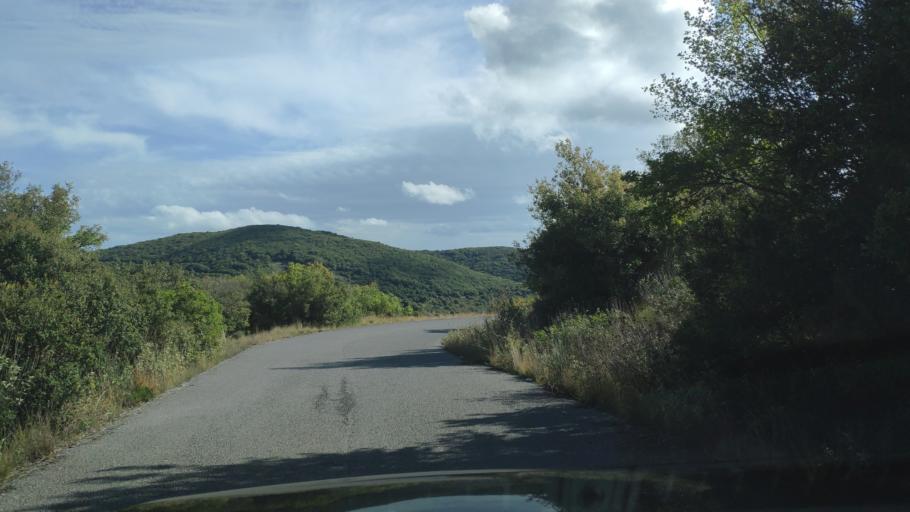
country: GR
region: Peloponnese
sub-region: Nomos Arkadias
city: Dimitsana
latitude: 37.5672
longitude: 22.0074
